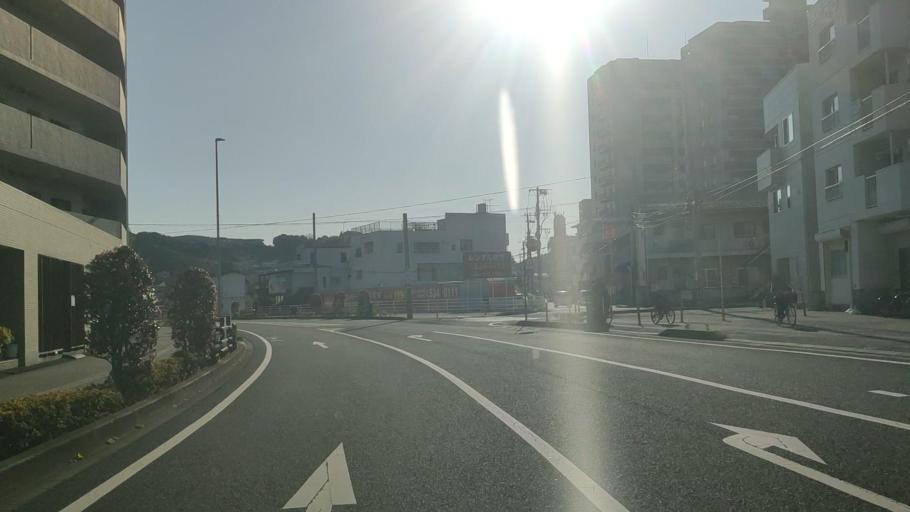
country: JP
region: Oita
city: Oita
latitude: 33.2304
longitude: 131.6014
